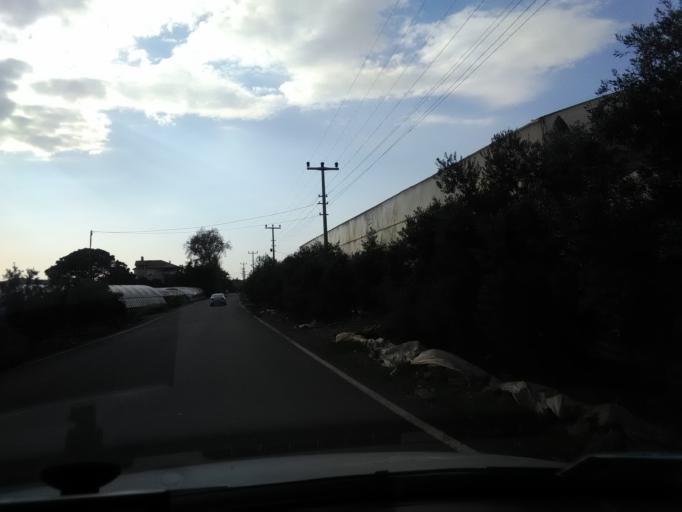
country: TR
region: Antalya
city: Gazipasa
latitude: 36.2726
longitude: 32.3365
